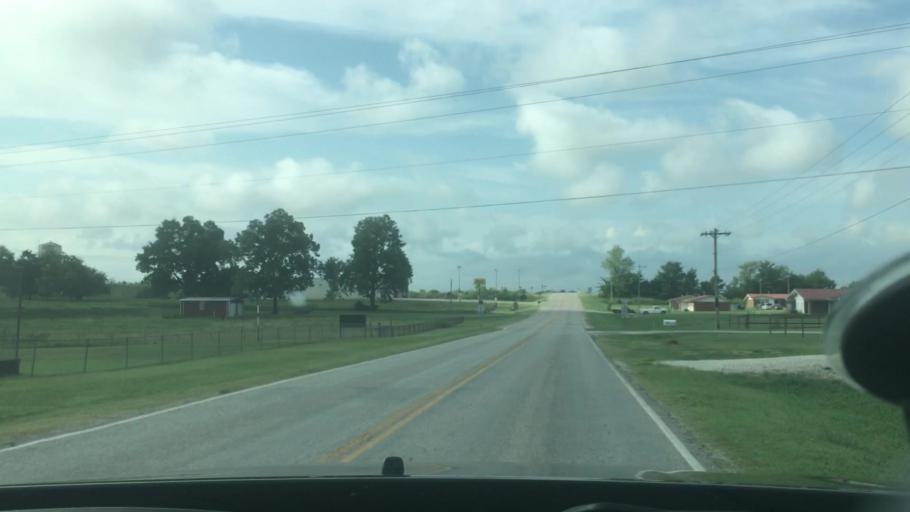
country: US
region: Oklahoma
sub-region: Pontotoc County
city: Ada
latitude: 34.6462
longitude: -96.5298
